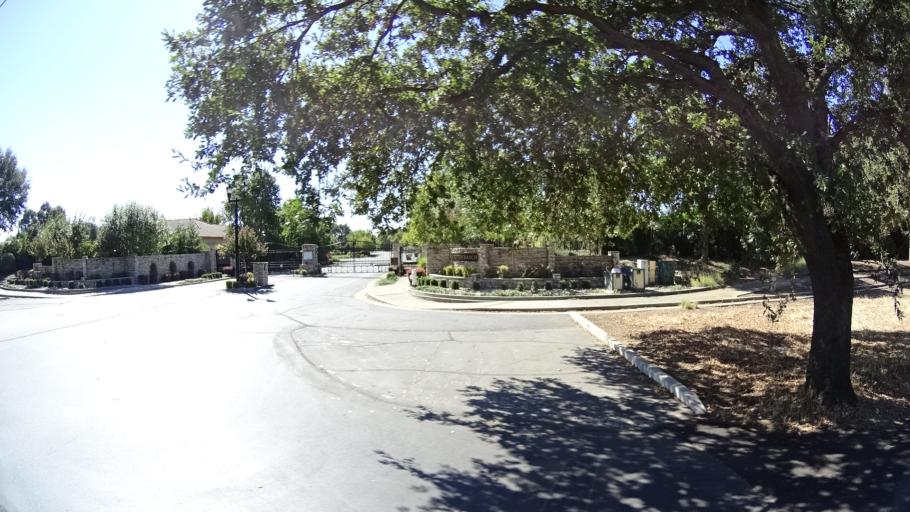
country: US
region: California
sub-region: Sacramento County
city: Vineyard
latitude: 38.4237
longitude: -121.3226
